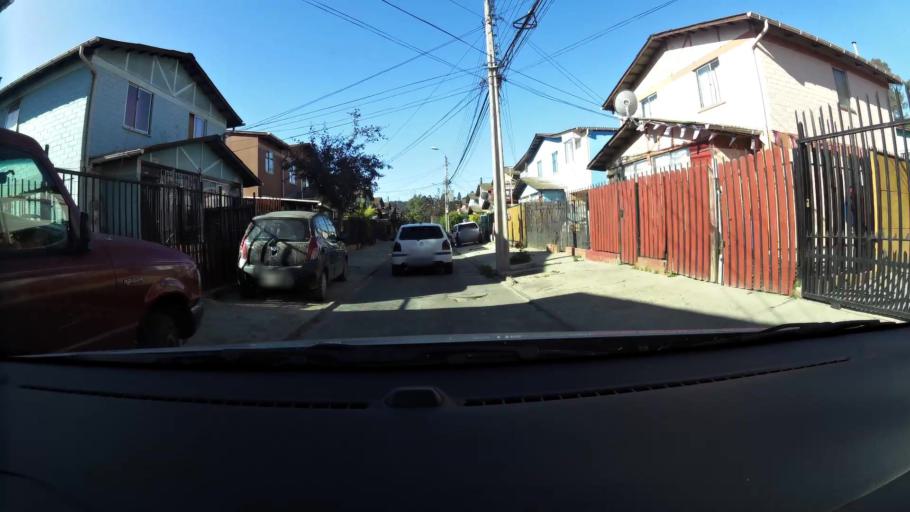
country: CL
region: Valparaiso
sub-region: Provincia de Valparaiso
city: Valparaiso
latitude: -33.1170
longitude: -71.5781
